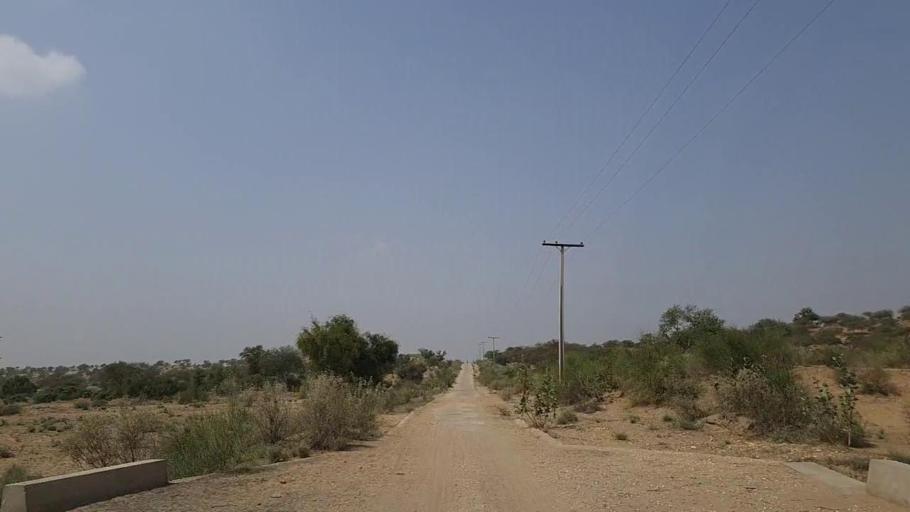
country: PK
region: Sindh
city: Mithi
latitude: 24.7677
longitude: 69.8949
